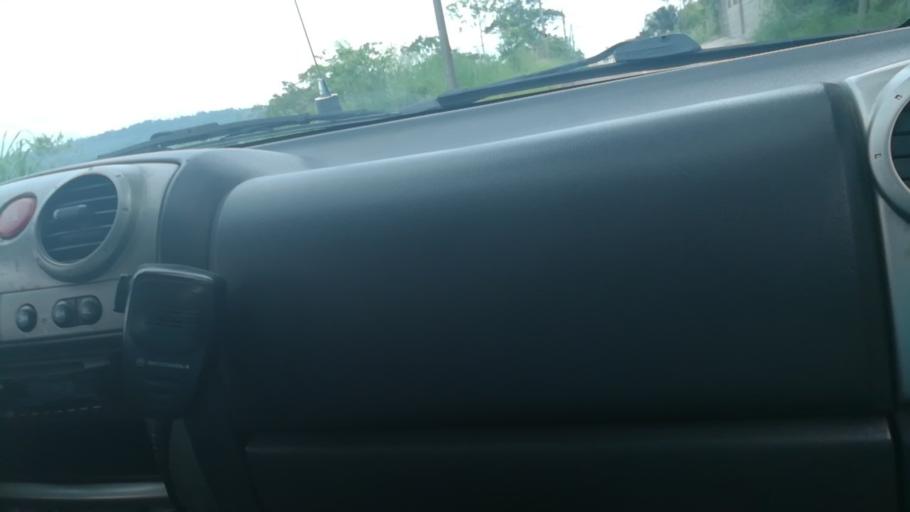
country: EC
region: Napo
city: Tena
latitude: -0.9777
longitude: -77.8152
